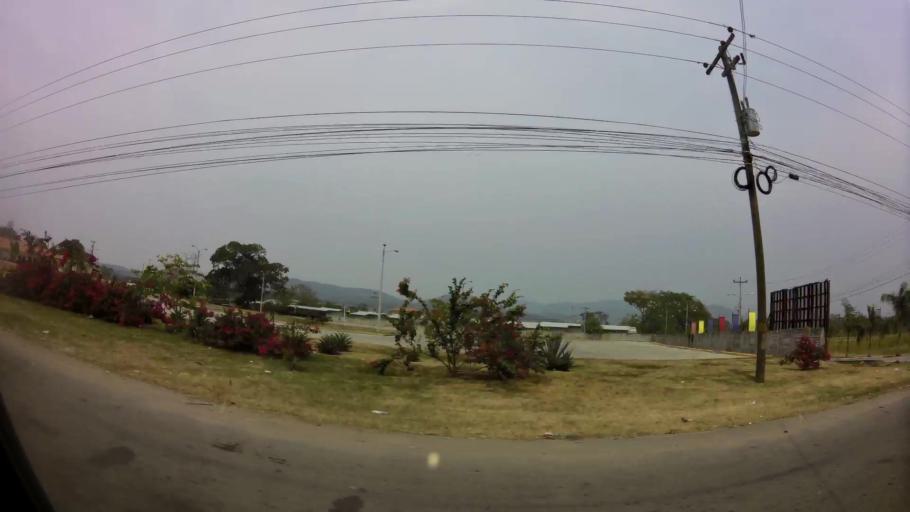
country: HN
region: Cortes
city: Villanueva
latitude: 15.3514
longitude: -87.9837
